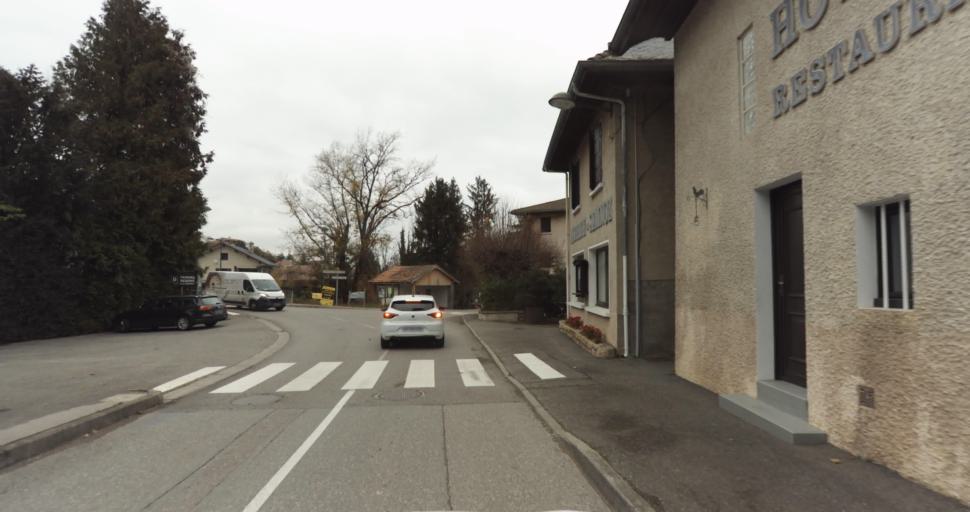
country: FR
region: Rhone-Alpes
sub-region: Departement de la Haute-Savoie
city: Saint-Jorioz
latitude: 45.8254
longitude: 6.1515
